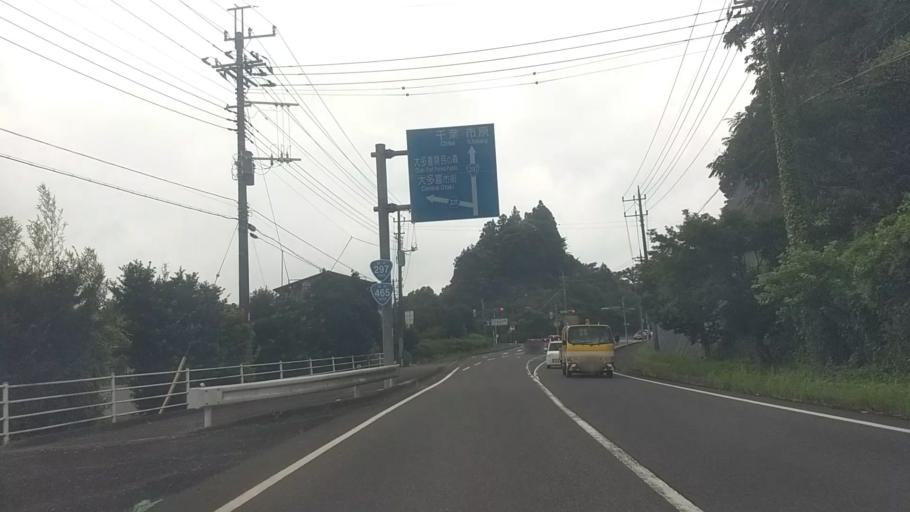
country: JP
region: Chiba
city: Ohara
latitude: 35.2724
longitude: 140.2531
